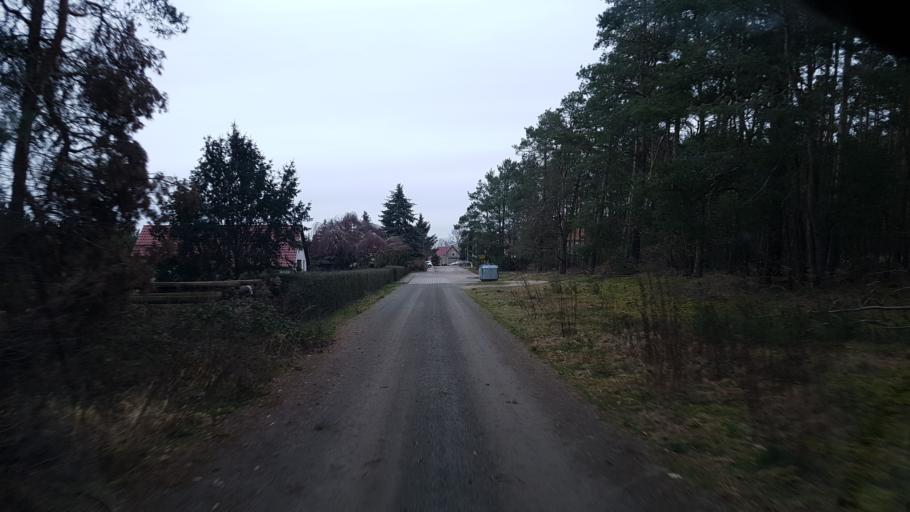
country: DE
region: Brandenburg
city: Herzberg
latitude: 51.7085
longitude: 13.3002
